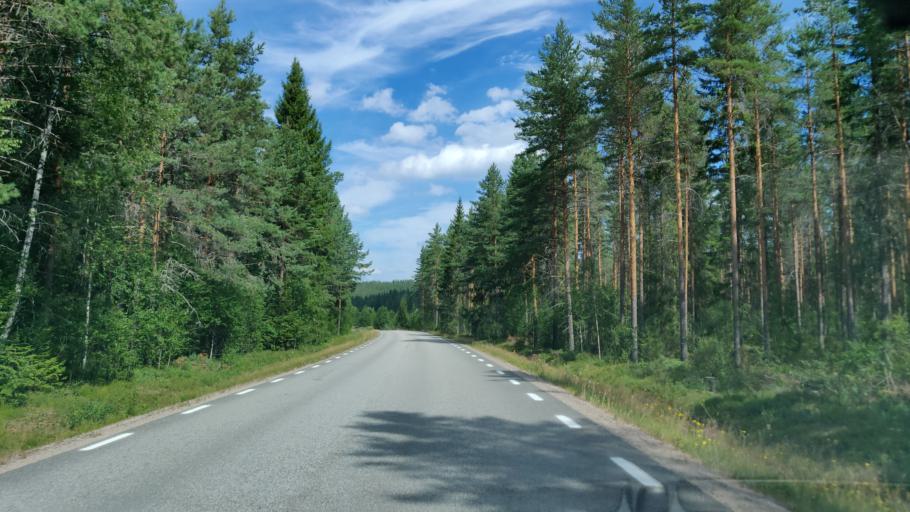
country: SE
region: Vaermland
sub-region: Hagfors Kommun
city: Ekshaerad
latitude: 60.0849
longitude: 13.5067
